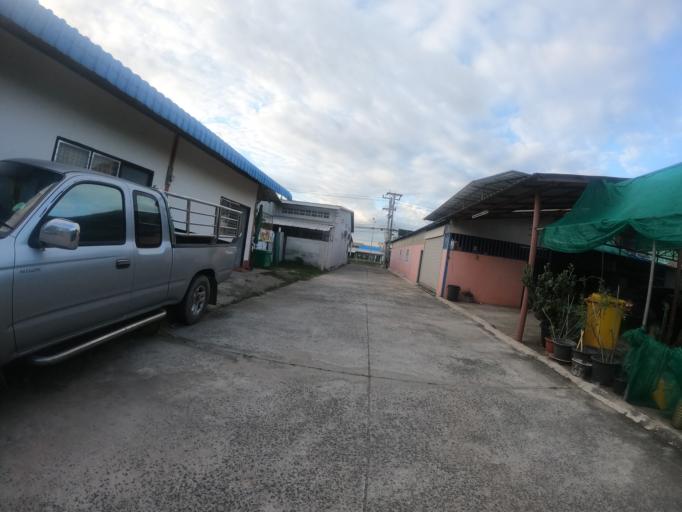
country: TH
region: Surin
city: Kap Choeng
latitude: 14.4522
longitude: 103.6925
